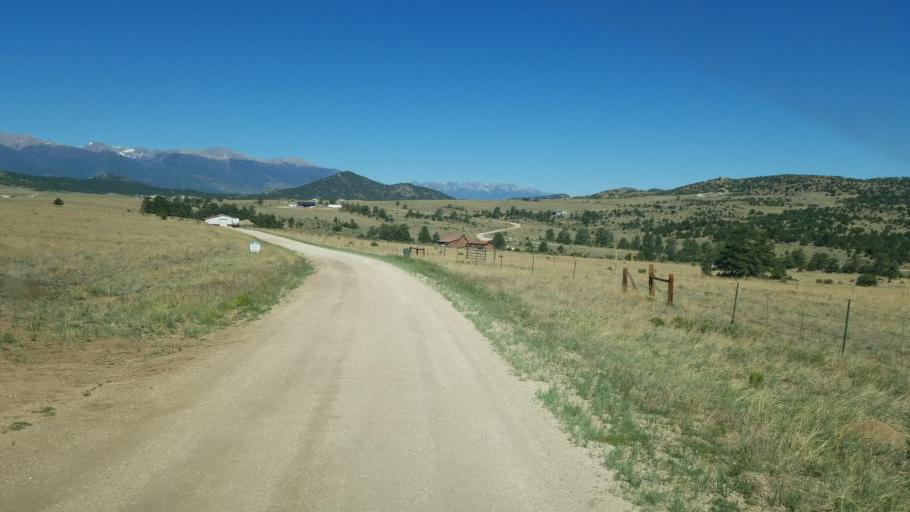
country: US
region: Colorado
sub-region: Custer County
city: Westcliffe
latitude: 38.2341
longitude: -105.4724
